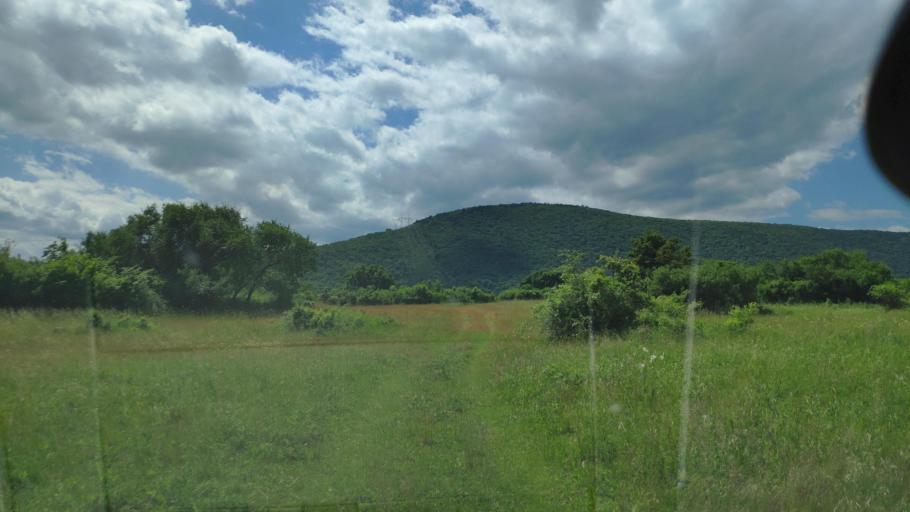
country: SK
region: Kosicky
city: Medzev
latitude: 48.6229
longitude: 20.8779
